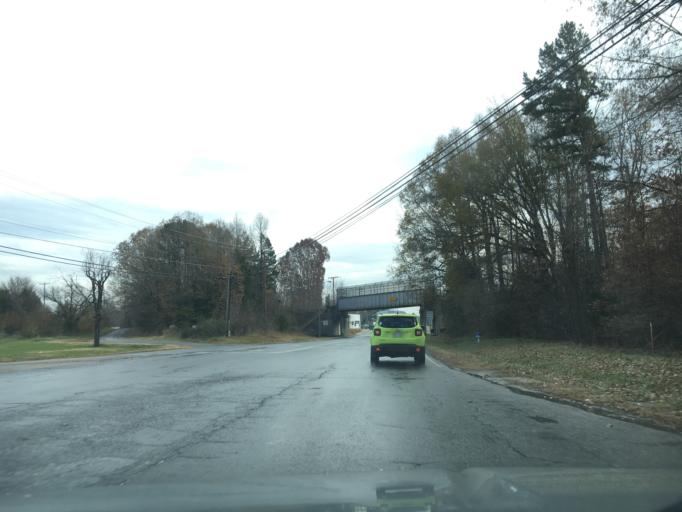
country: US
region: Virginia
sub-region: Prince Edward County
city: Farmville
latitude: 37.3131
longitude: -78.4224
